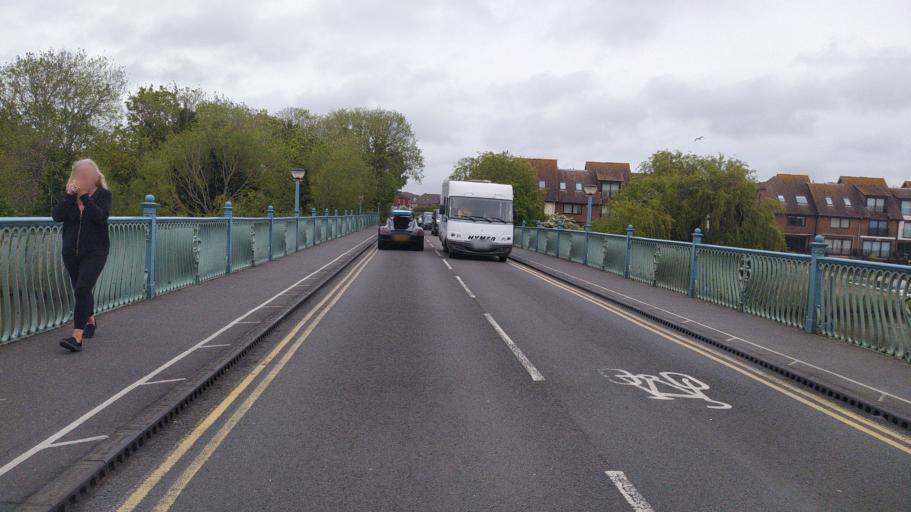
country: GB
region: England
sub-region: Dorset
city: Christchurch
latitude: 50.7297
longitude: -1.7897
